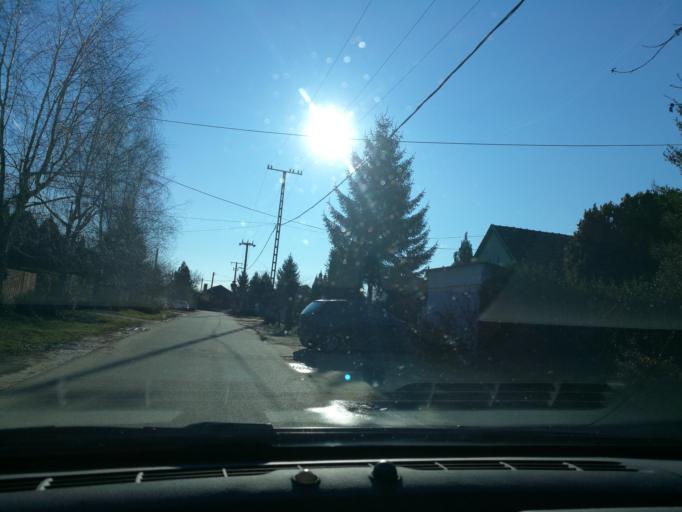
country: HU
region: Szabolcs-Szatmar-Bereg
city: Nyiregyhaza
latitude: 47.9482
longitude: 21.7516
